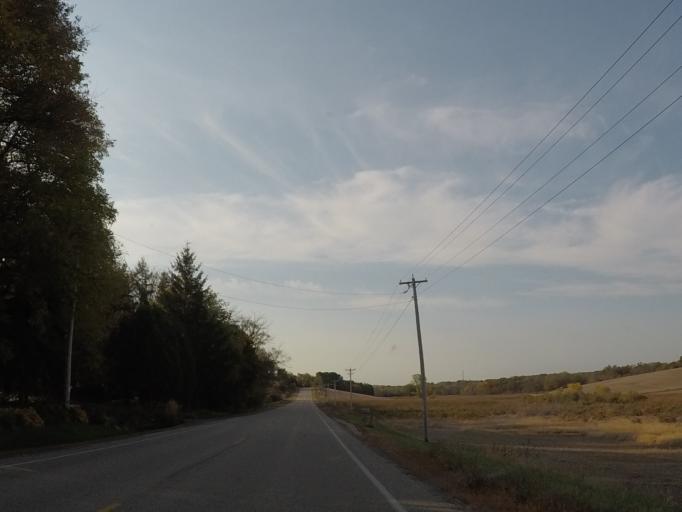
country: US
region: Wisconsin
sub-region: Dane County
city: Cross Plains
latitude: 43.0374
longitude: -89.6164
